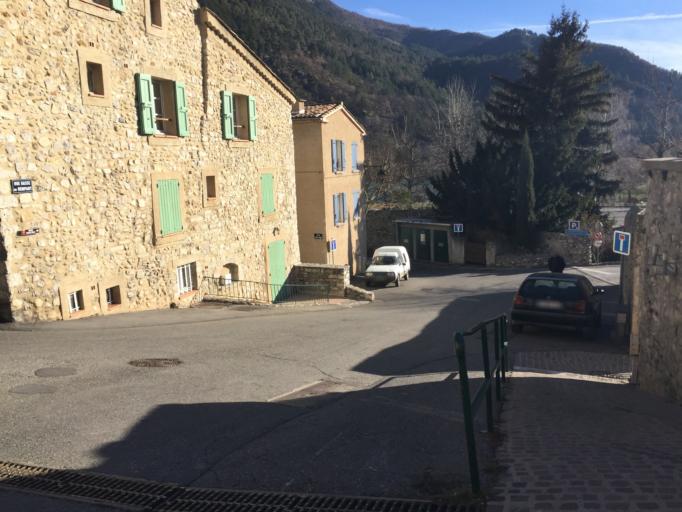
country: FR
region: Provence-Alpes-Cote d'Azur
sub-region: Departement des Alpes-de-Haute-Provence
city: Sisteron
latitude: 44.1963
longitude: 5.9453
